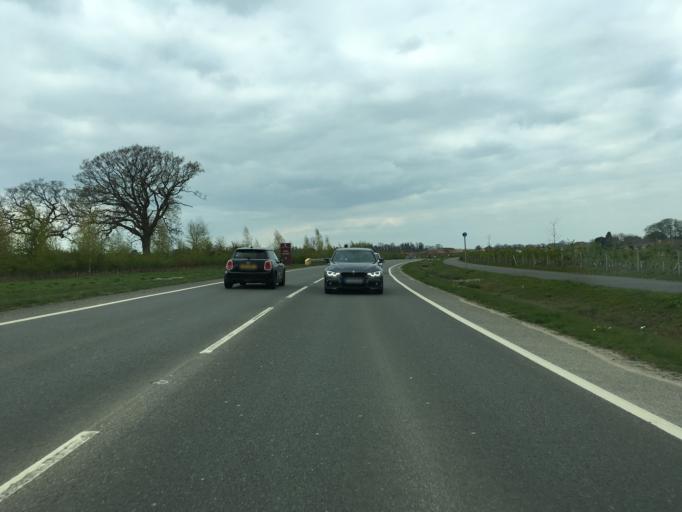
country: GB
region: England
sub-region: Oxfordshire
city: Bicester
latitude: 51.8892
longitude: -1.1758
